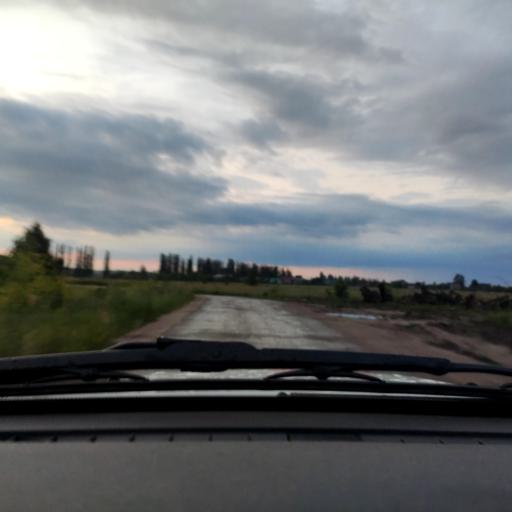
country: RU
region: Voronezj
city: Maslovka
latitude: 51.5155
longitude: 39.2272
